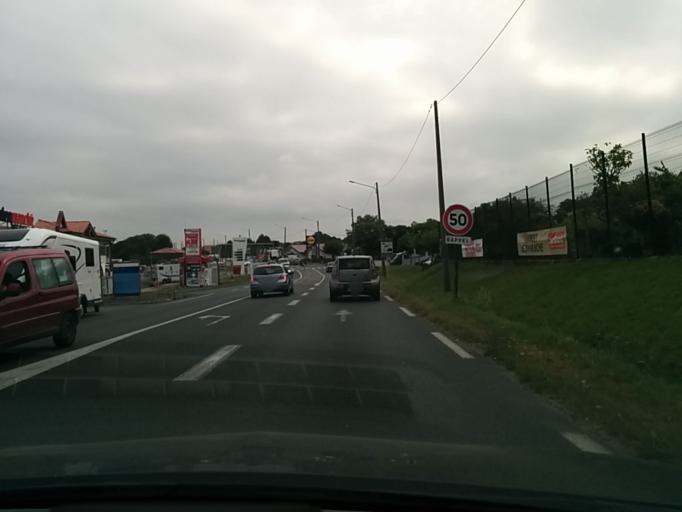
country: FR
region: Aquitaine
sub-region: Departement des Pyrenees-Atlantiques
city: Bidart
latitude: 43.4472
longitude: -1.5754
